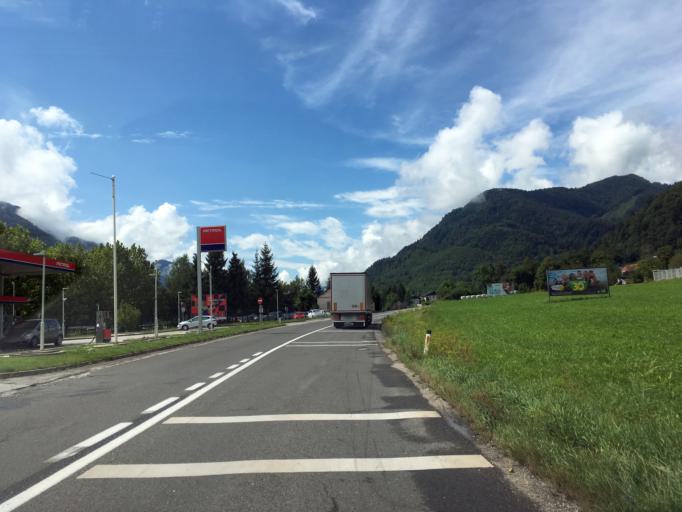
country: SI
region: Jesenice
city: Slovenski Javornik
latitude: 46.4227
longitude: 14.1032
